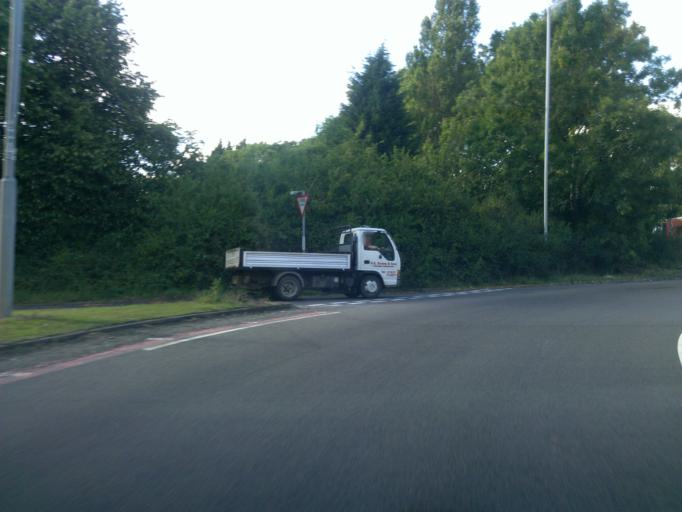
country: GB
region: England
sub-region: Warwickshire
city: Atherstone
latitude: 52.5720
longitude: -1.5272
